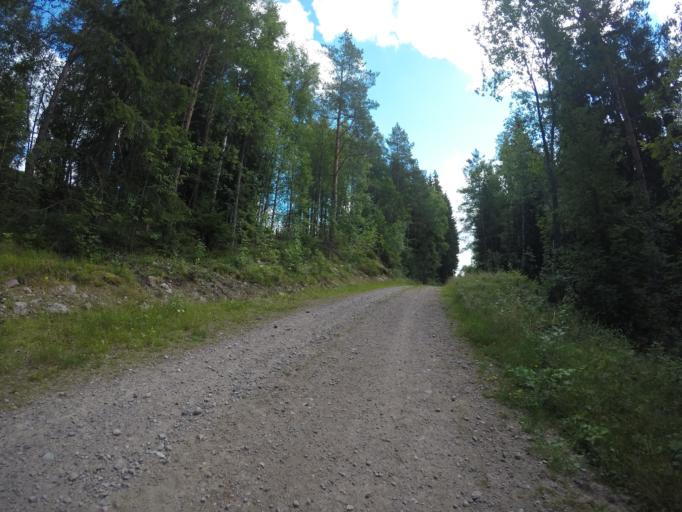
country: SE
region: Vaermland
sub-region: Filipstads Kommun
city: Lesjofors
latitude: 60.0693
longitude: 14.4600
